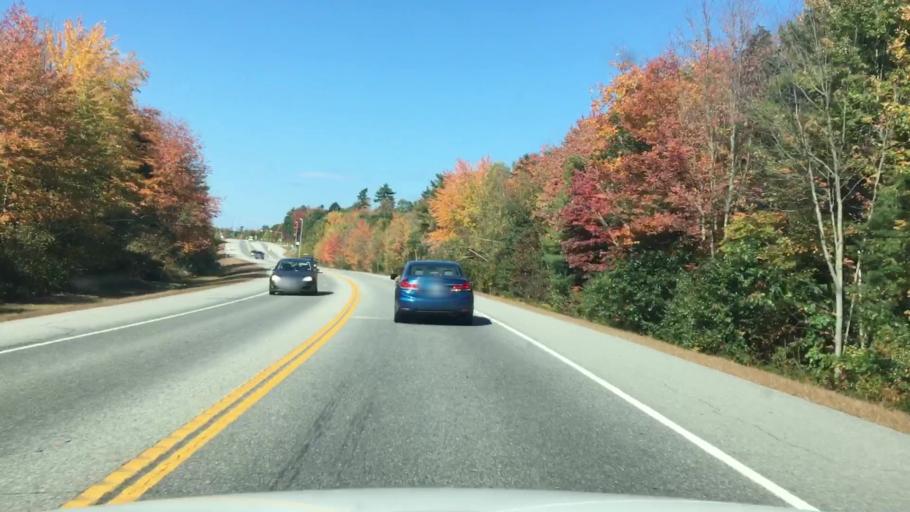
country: US
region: Maine
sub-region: Cumberland County
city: Brunswick
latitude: 43.9344
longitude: -69.9515
